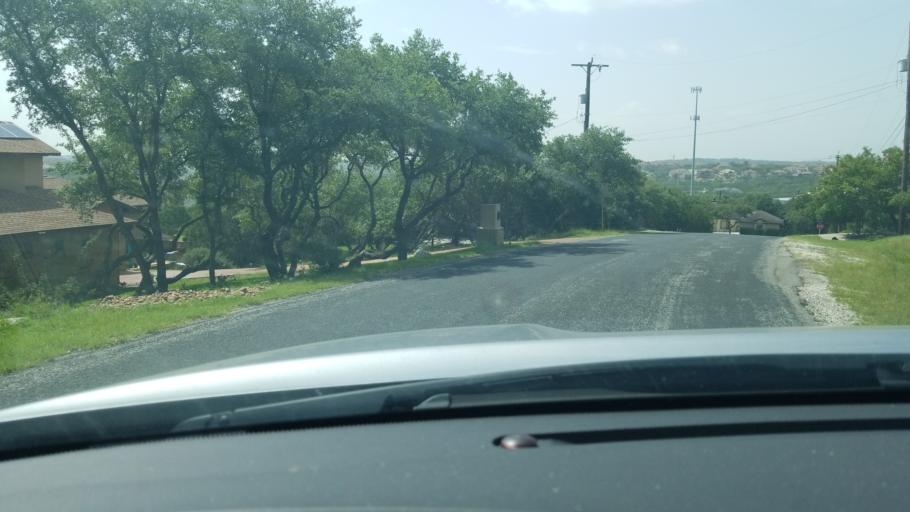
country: US
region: Texas
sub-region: Bexar County
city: Timberwood Park
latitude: 29.6857
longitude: -98.4918
